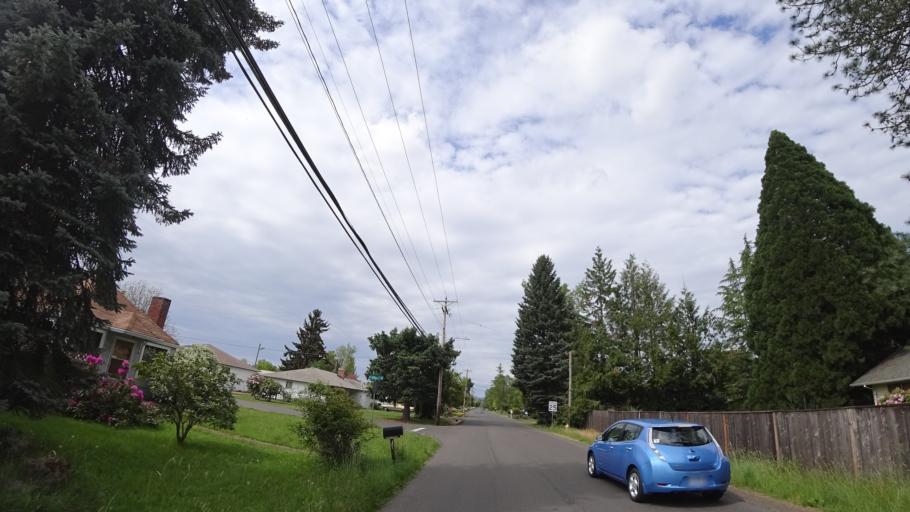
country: US
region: Oregon
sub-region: Washington County
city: Aloha
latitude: 45.5026
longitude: -122.9227
